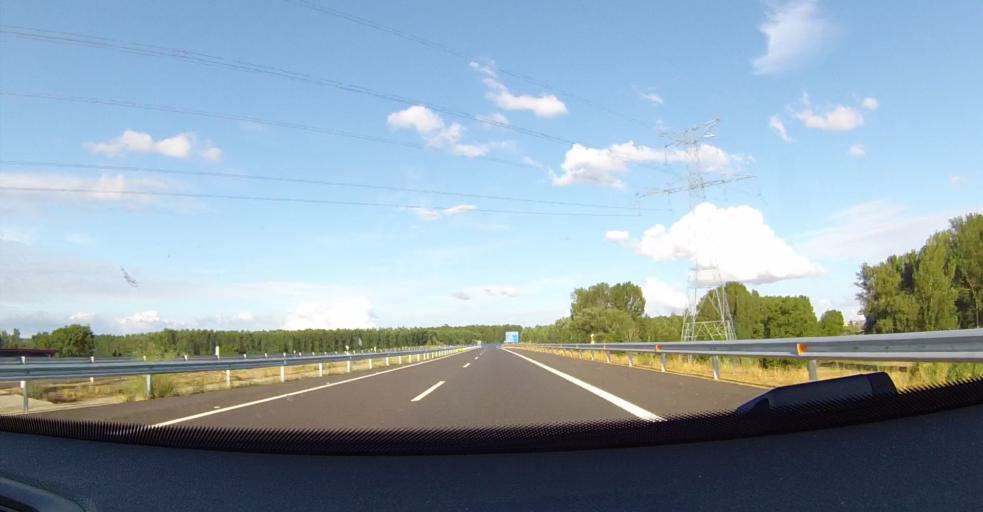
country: ES
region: Castille and Leon
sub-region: Provincia de Leon
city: Mansilla de las Mulas
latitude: 42.5104
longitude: -5.4077
